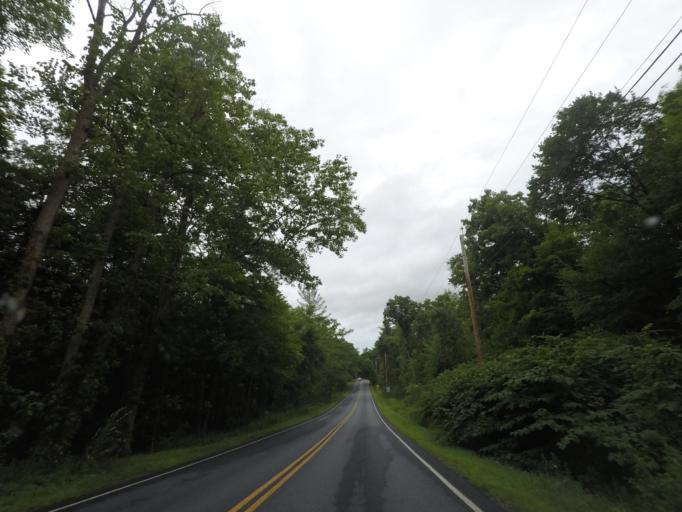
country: US
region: New York
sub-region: Rensselaer County
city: West Sand Lake
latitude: 42.5996
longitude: -73.5957
